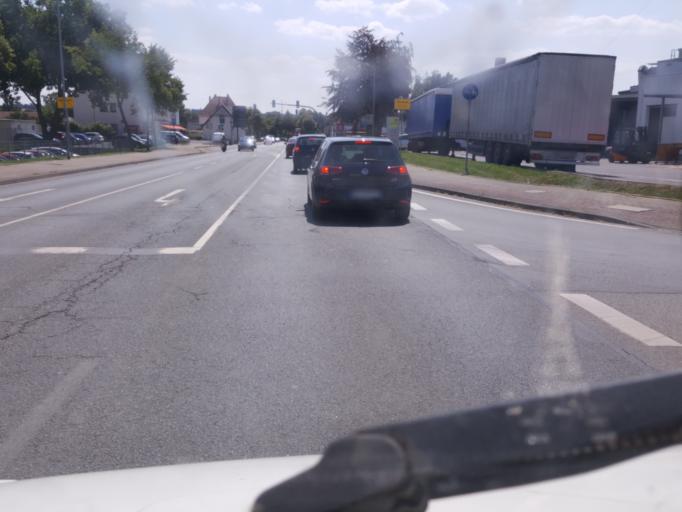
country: DE
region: North Rhine-Westphalia
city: Loehne
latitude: 52.2075
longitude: 8.7139
